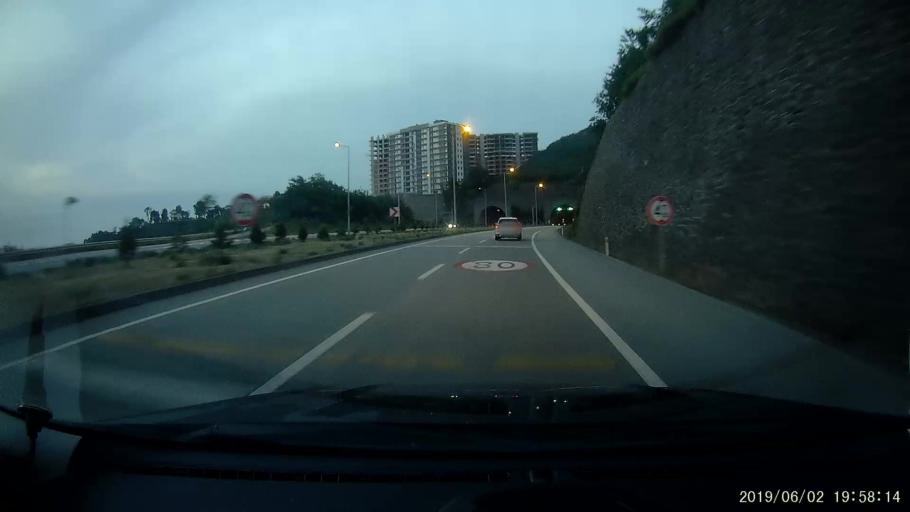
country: TR
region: Giresun
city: Tirebolu
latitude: 40.9968
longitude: 38.7936
